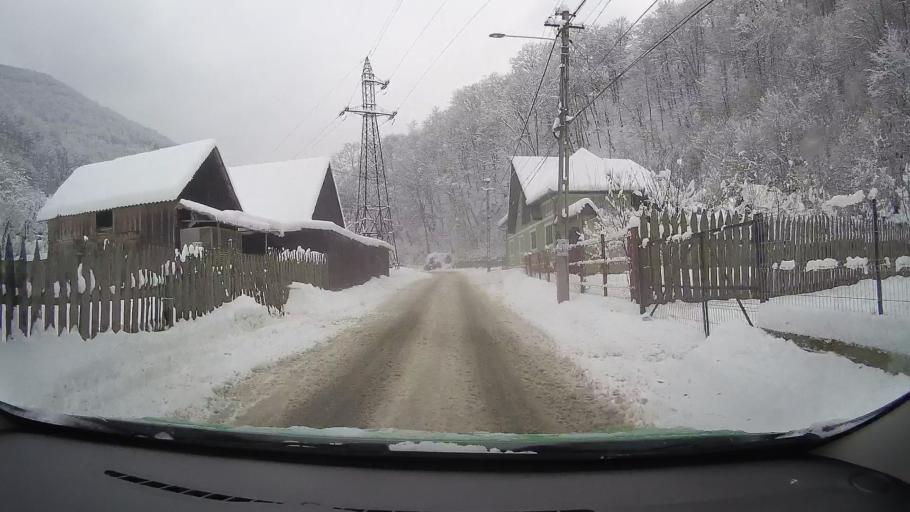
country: RO
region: Alba
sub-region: Comuna Sugag
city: Dobra
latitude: 45.7619
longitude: 23.6566
